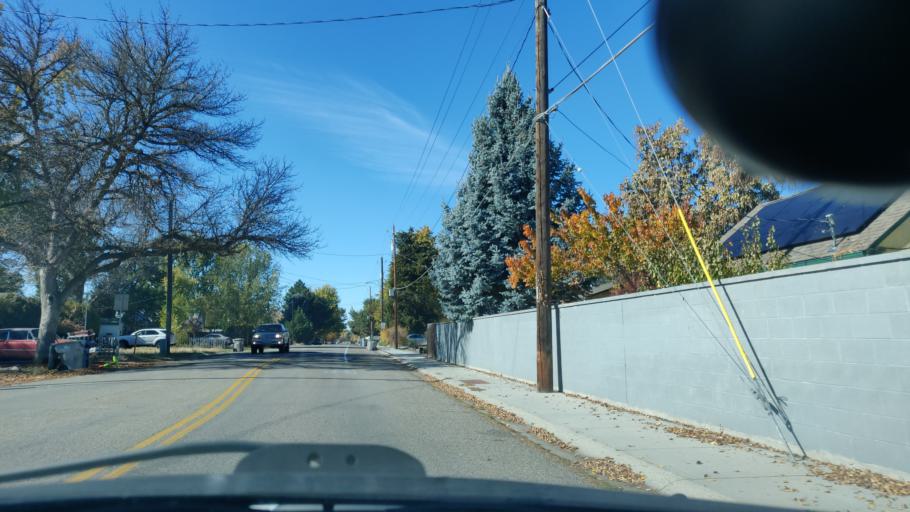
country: US
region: Idaho
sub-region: Ada County
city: Garden City
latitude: 43.5934
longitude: -116.2339
